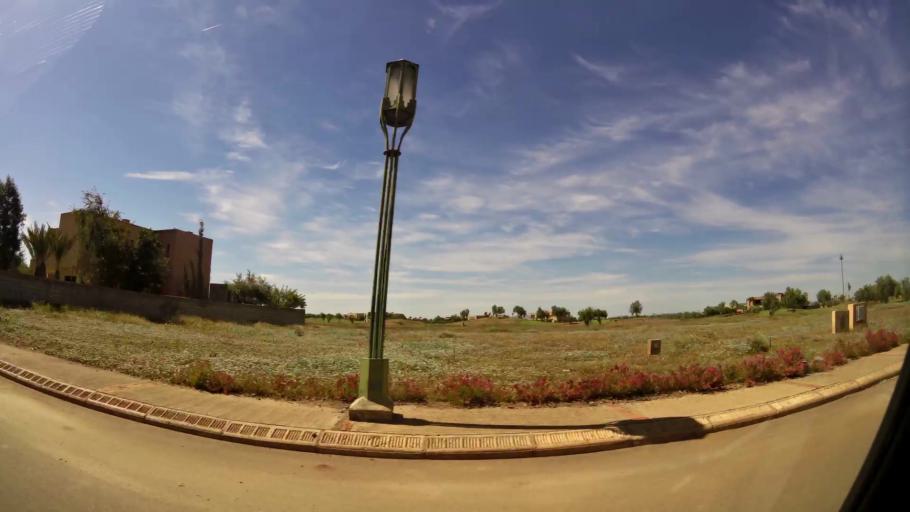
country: MA
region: Marrakech-Tensift-Al Haouz
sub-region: Marrakech
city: Marrakesh
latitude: 31.6192
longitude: -7.9234
